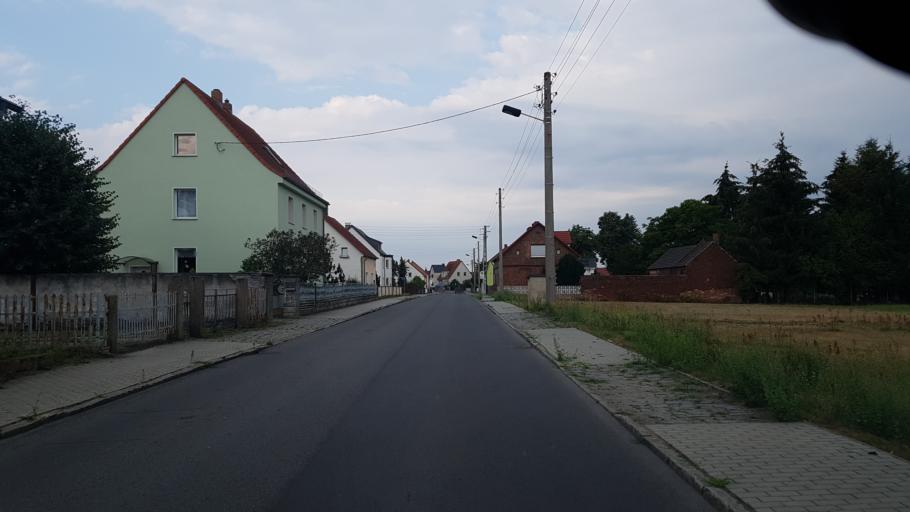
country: DE
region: Brandenburg
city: Lauchhammer
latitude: 51.4782
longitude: 13.7402
